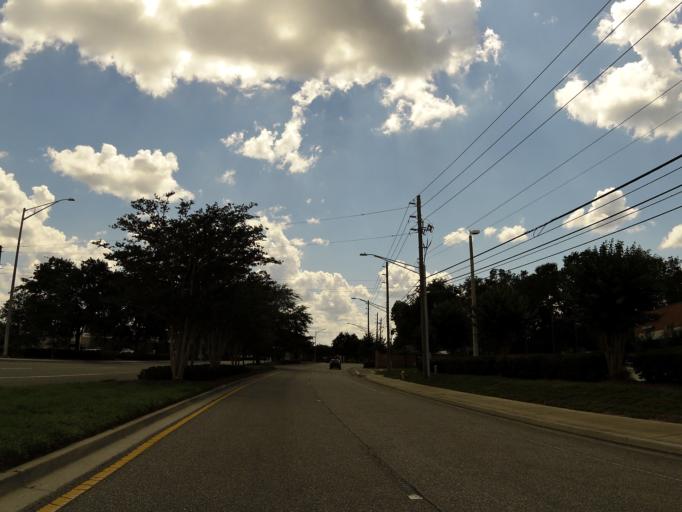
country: US
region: Florida
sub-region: Saint Johns County
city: Fruit Cove
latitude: 30.1407
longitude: -81.5223
